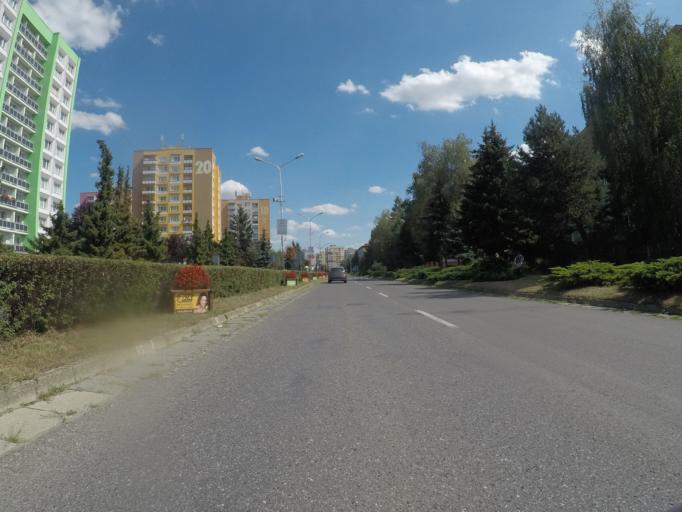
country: SK
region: Banskobystricky
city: Rimavska Sobota
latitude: 48.3839
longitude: 20.0117
